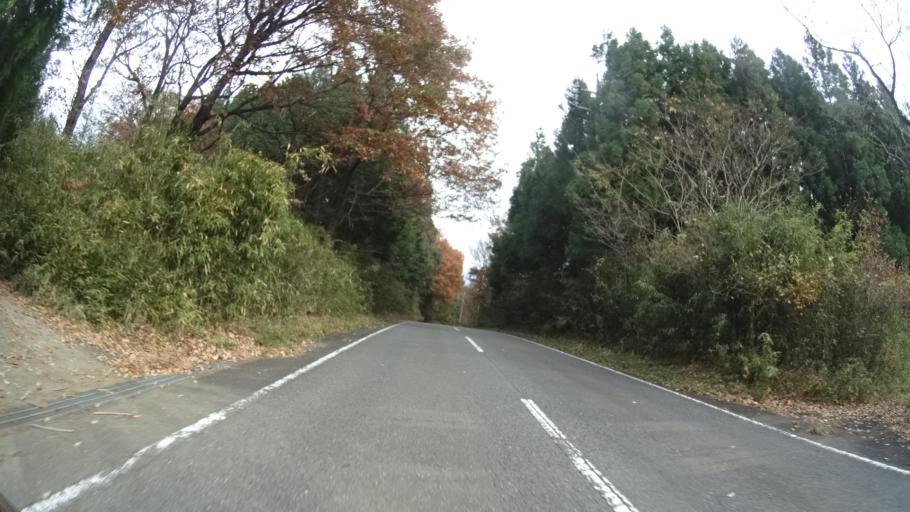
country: JP
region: Gunma
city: Omamacho-omama
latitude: 36.4755
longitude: 139.1611
